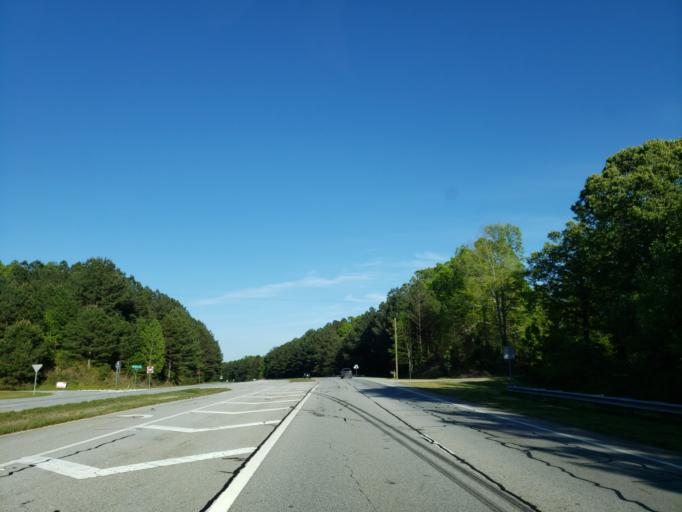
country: US
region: Georgia
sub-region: Paulding County
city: Dallas
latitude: 33.9124
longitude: -84.9023
